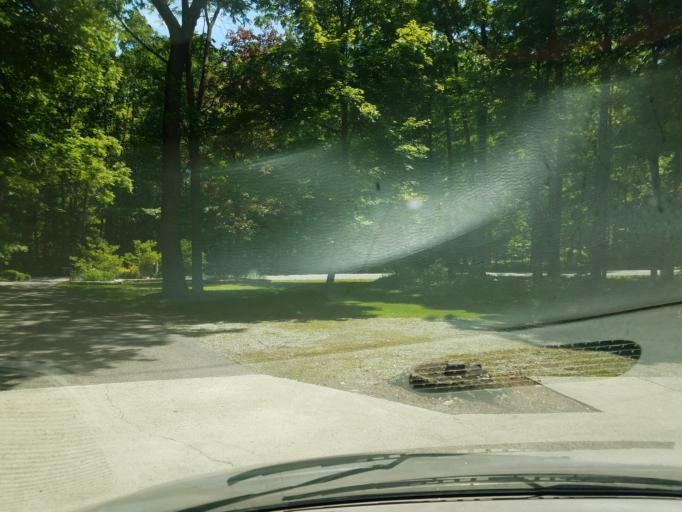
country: US
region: Ohio
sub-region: Delaware County
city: Powell
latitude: 40.2135
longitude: -83.0695
